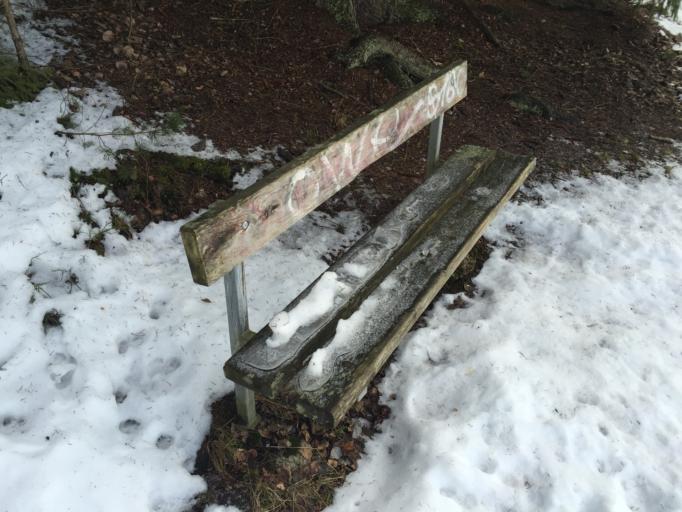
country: SE
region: Stockholm
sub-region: Botkyrka Kommun
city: Varsta
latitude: 59.1896
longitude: 17.7693
